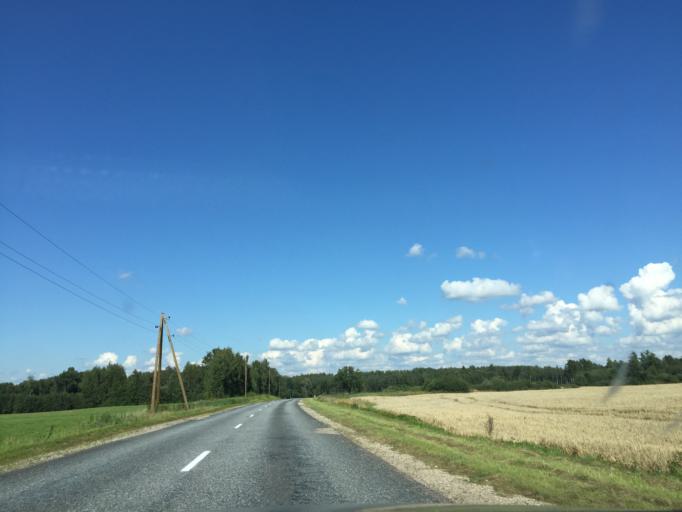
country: LV
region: Limbazu Rajons
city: Limbazi
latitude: 57.4349
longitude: 24.7161
